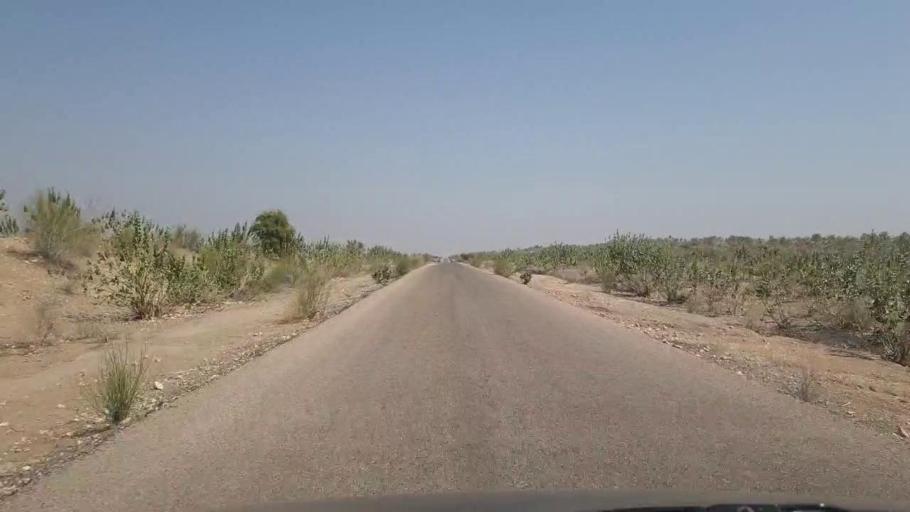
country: PK
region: Sindh
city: Chor
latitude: 25.6818
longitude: 70.1785
